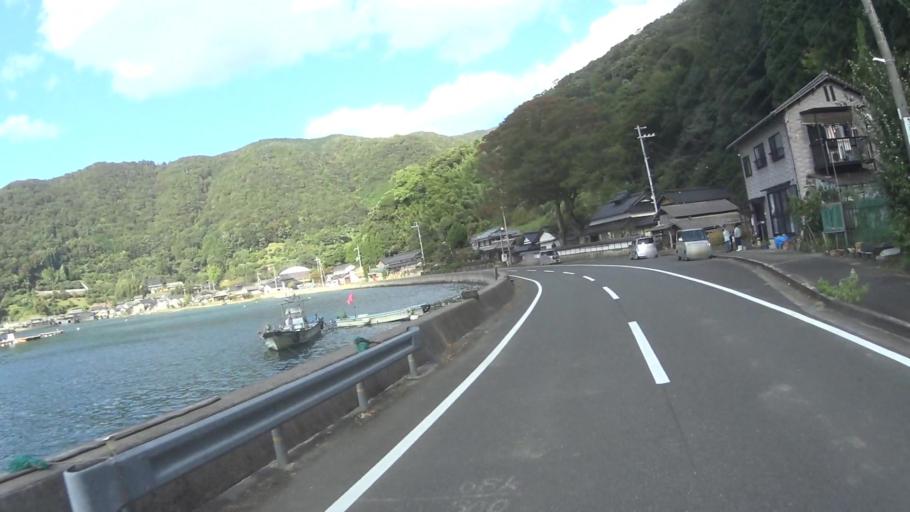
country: JP
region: Kyoto
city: Maizuru
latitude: 35.5169
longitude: 135.3496
